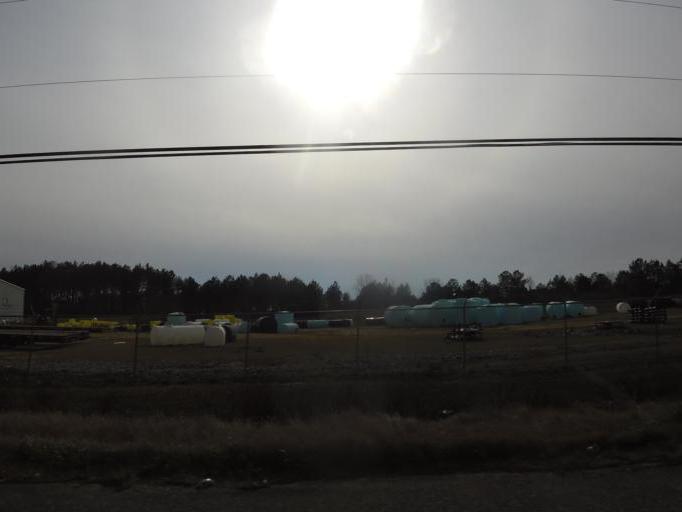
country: US
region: Alabama
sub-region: Houston County
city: Cowarts
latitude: 31.1957
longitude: -85.3316
